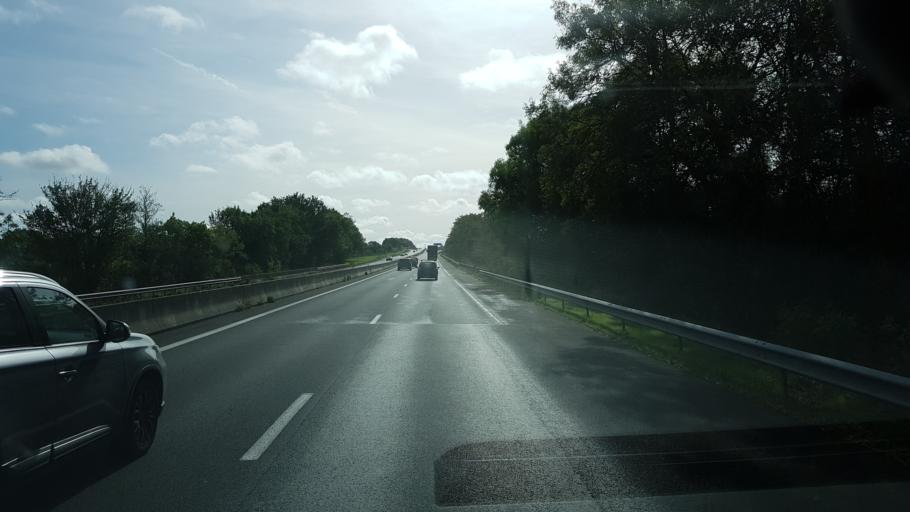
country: FR
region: Centre
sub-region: Departement de l'Indre
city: Argenton-sur-Creuse
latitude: 46.5560
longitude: 1.5061
